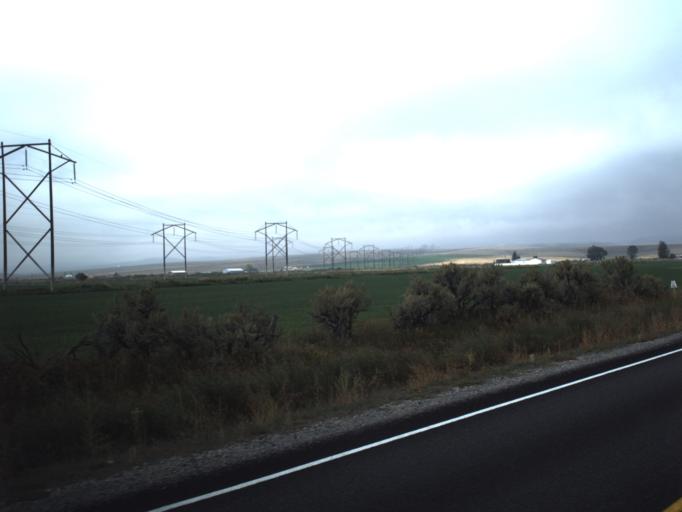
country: US
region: Utah
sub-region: Rich County
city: Randolph
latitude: 41.5174
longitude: -111.1525
